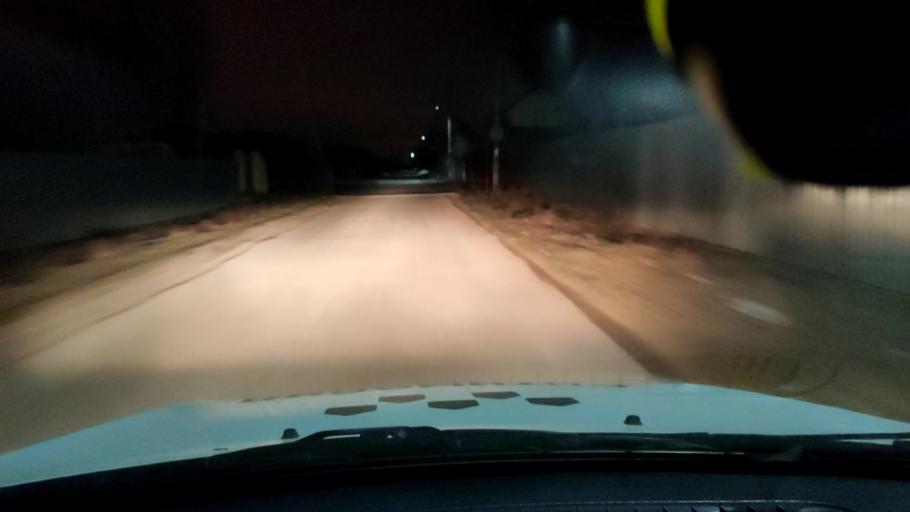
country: RU
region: Samara
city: Podstepki
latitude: 53.5159
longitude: 49.0751
